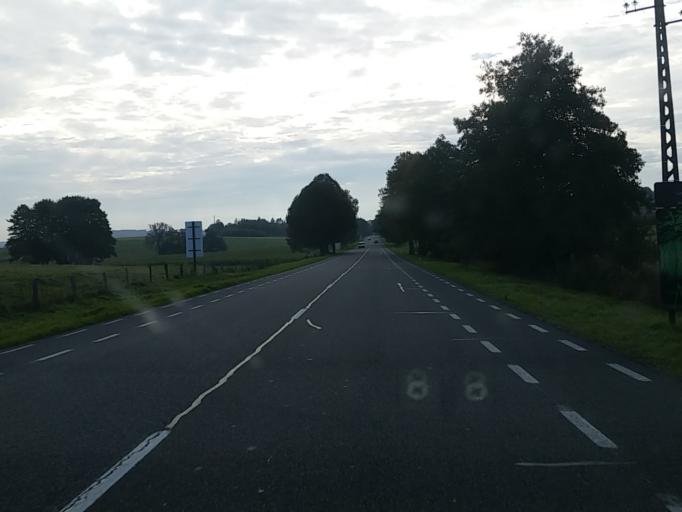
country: BE
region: Wallonia
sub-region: Province du Luxembourg
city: Herbeumont
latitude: 49.7239
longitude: 5.2417
